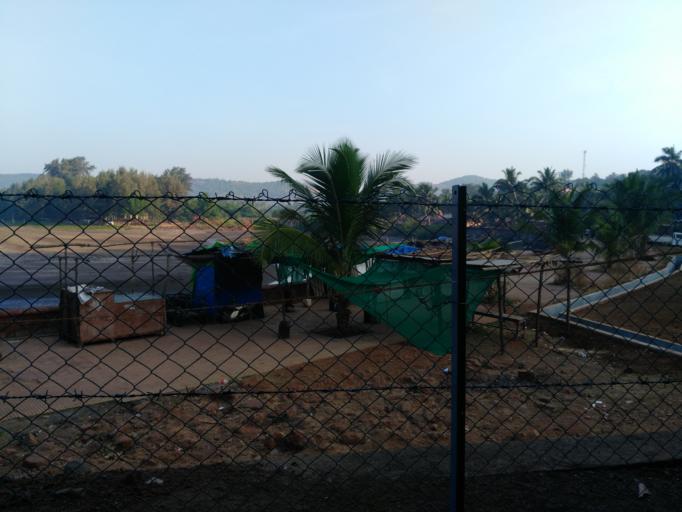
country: IN
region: Maharashtra
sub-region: Raigarh
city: Srivardhan
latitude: 17.9925
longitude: 73.0212
